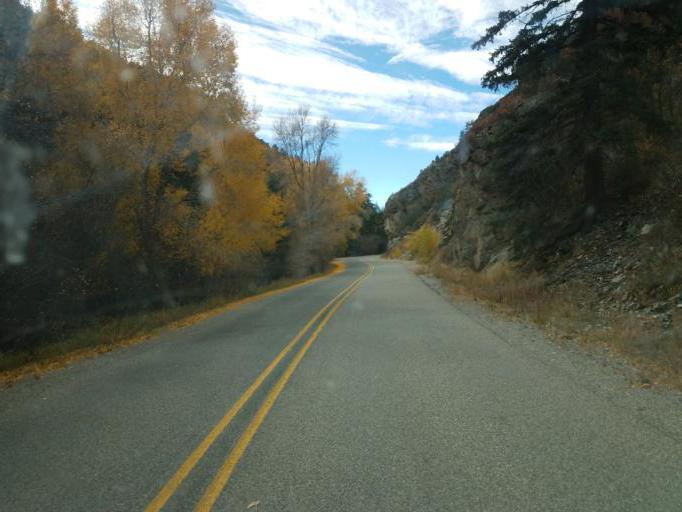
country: US
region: New Mexico
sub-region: Taos County
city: Arroyo Seco
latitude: 36.5430
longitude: -105.5558
